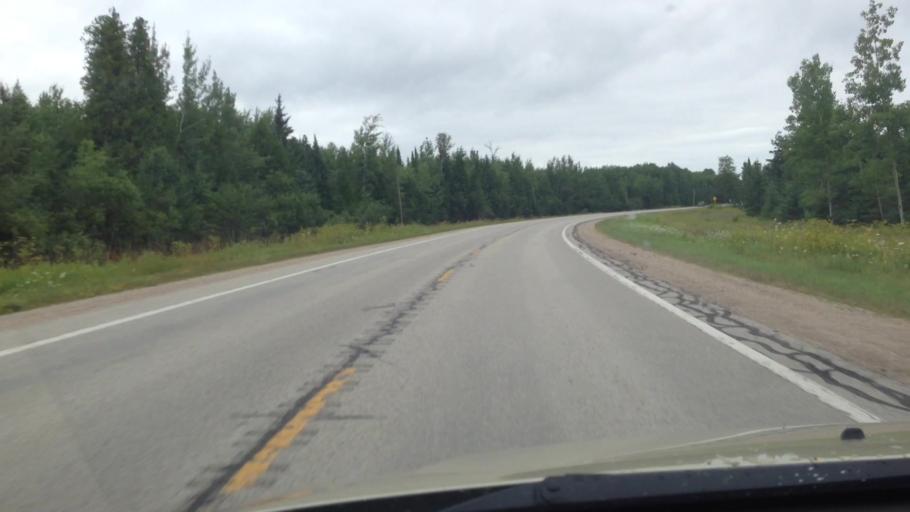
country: US
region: Michigan
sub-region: Delta County
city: Escanaba
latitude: 45.5546
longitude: -87.2685
